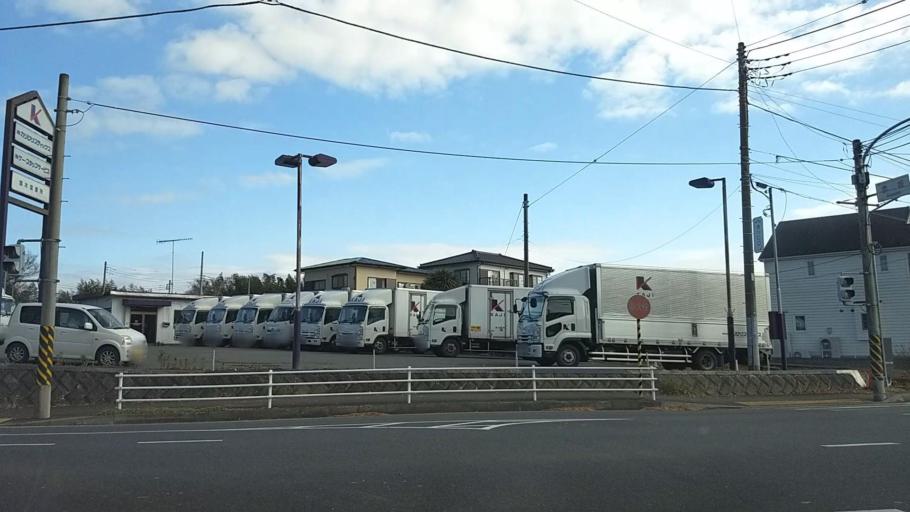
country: JP
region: Kanagawa
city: Atsugi
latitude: 35.4274
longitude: 139.3283
